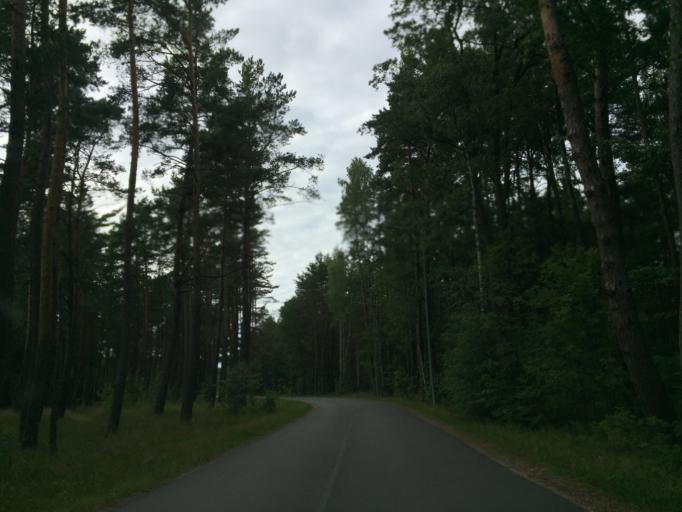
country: LV
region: Carnikava
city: Carnikava
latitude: 57.1339
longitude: 24.2509
